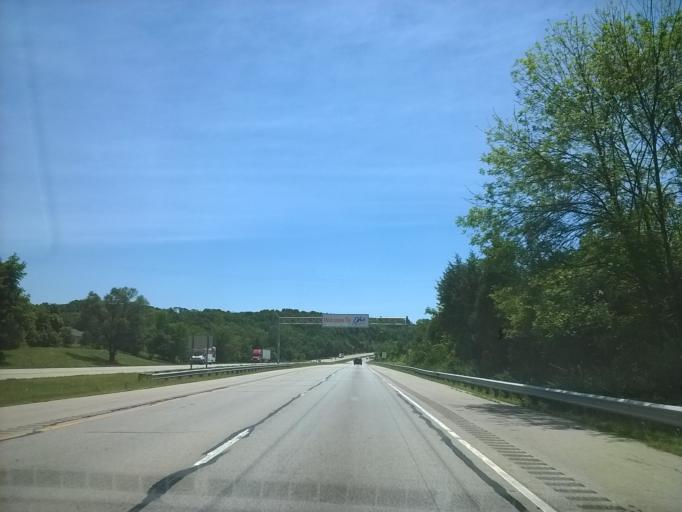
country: US
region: Ohio
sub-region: Hamilton County
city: Harrison
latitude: 39.2765
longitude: -84.8203
